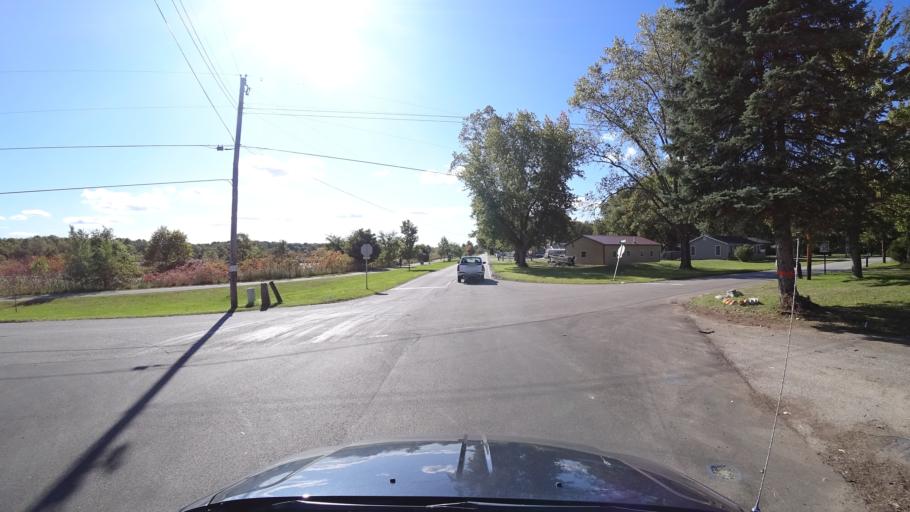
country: US
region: Indiana
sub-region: LaPorte County
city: Michigan City
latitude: 41.6904
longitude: -86.9132
